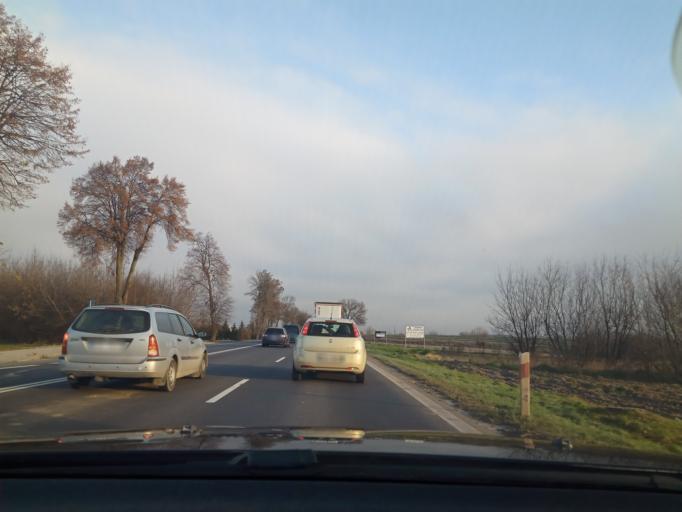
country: PL
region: Lesser Poland Voivodeship
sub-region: Powiat miechowski
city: Miechow
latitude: 50.3007
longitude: 20.0359
